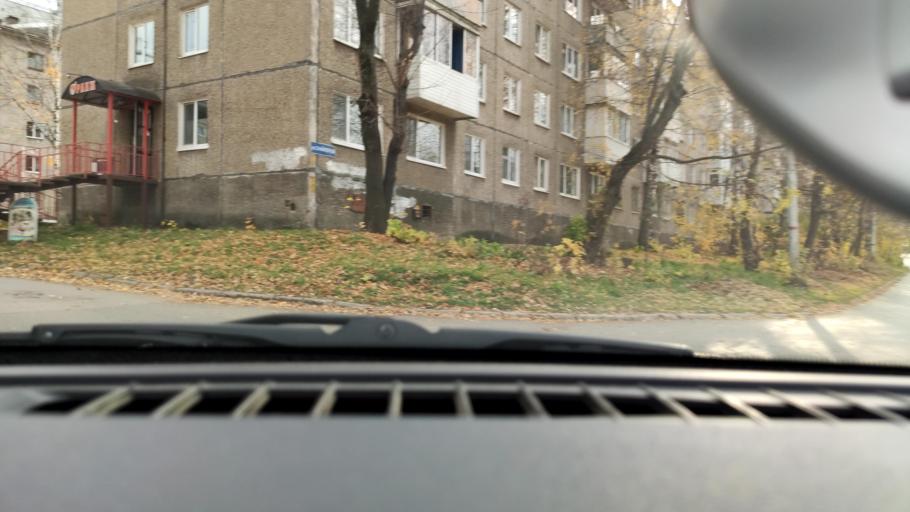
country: RU
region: Perm
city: Perm
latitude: 57.9811
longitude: 56.2119
